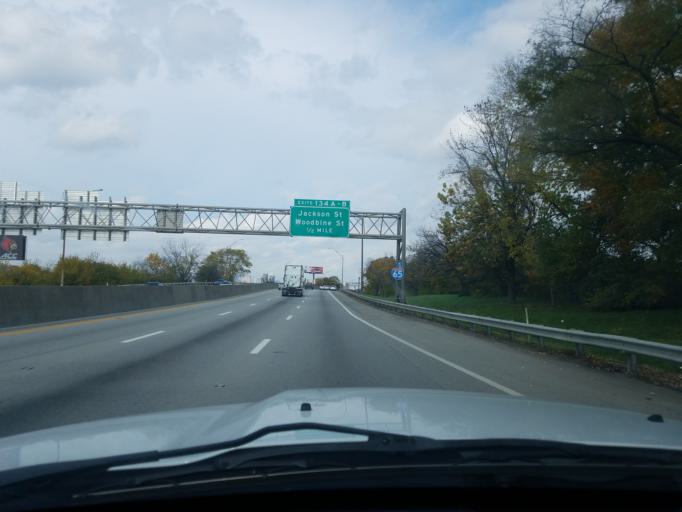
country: US
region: Kentucky
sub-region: Jefferson County
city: Audubon Park
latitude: 38.2166
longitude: -85.7521
